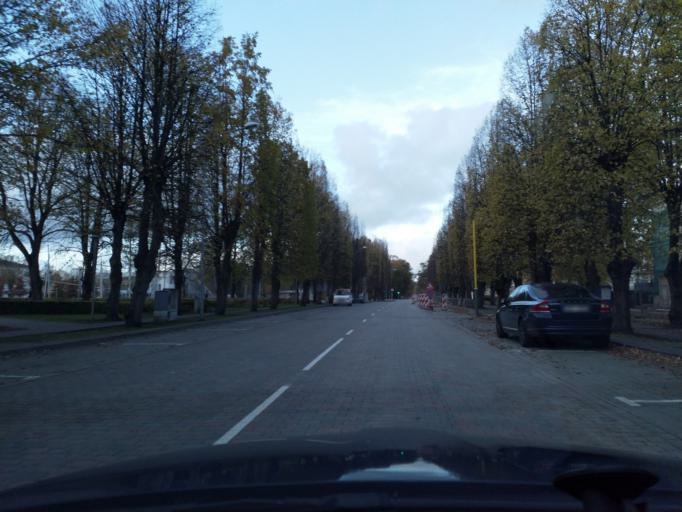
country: LV
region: Ventspils
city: Ventspils
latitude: 57.3879
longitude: 21.5653
